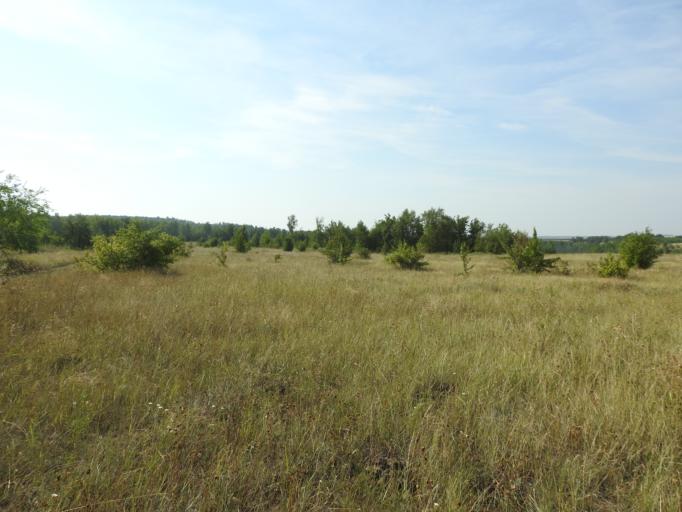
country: RU
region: Saratov
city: Kamenskiy
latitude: 50.6524
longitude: 45.5944
